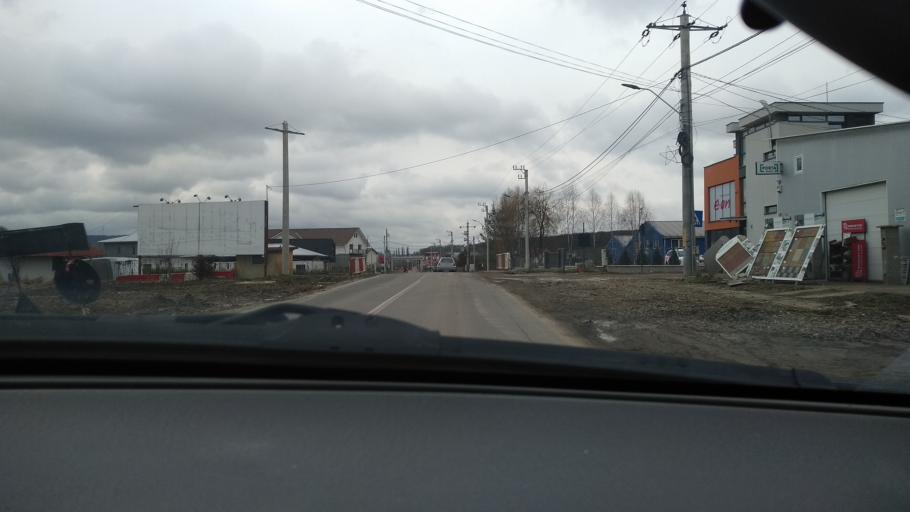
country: RO
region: Mures
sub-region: Comuna Livezeni
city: Livezeni
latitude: 46.5444
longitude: 24.6182
